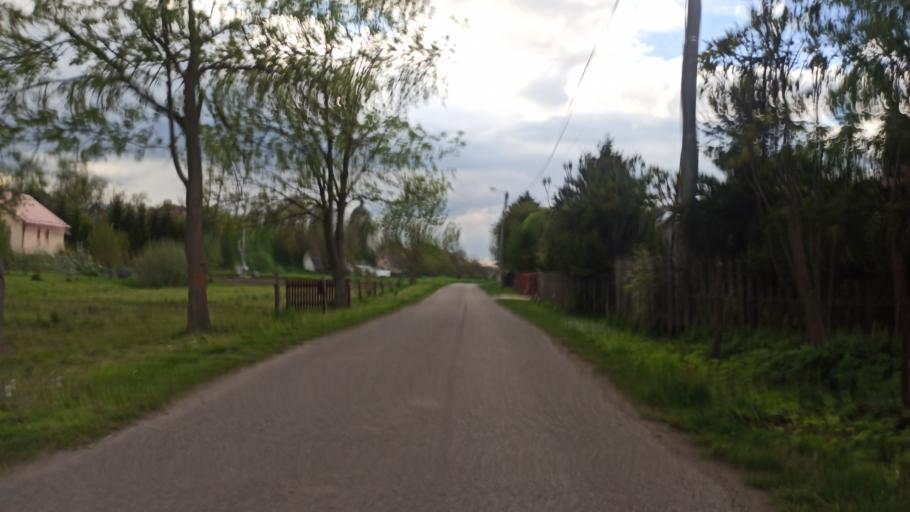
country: PL
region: Subcarpathian Voivodeship
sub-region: Powiat jaroslawski
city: Sosnica
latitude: 49.9236
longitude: 22.8596
